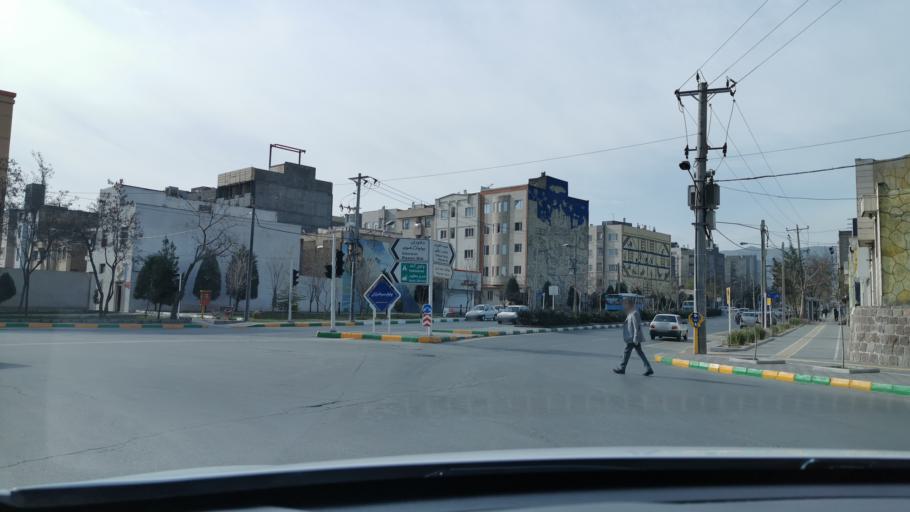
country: IR
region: Razavi Khorasan
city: Mashhad
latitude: 36.3047
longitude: 59.5125
